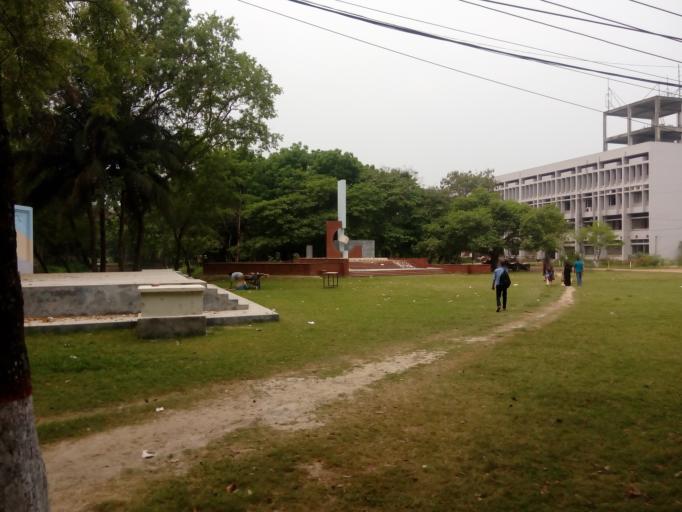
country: BD
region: Khulna
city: Khulna
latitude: 22.8017
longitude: 89.5340
